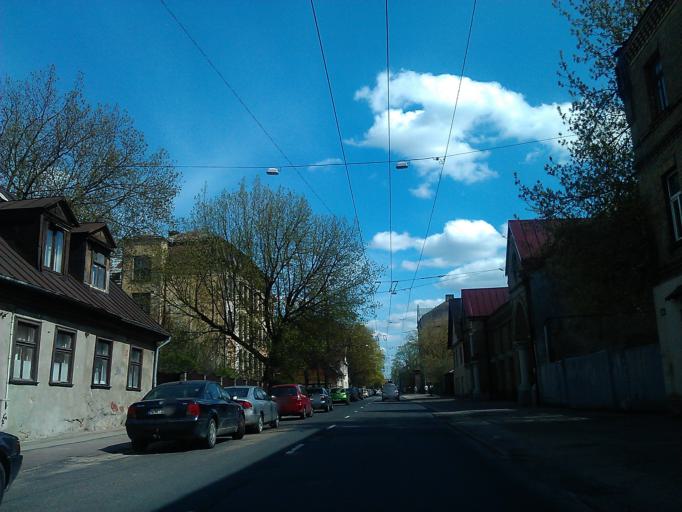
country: LV
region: Riga
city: Riga
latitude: 56.9407
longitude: 24.1421
